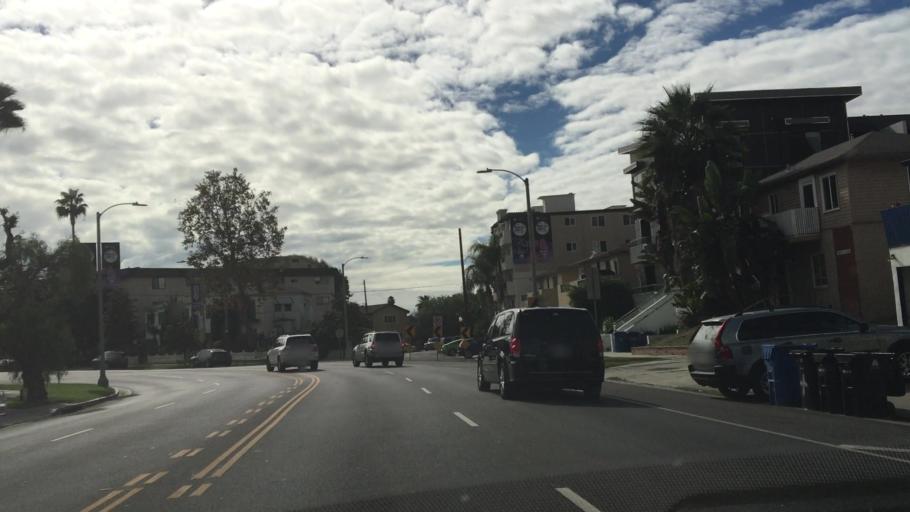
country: US
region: California
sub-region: Los Angeles County
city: Century City
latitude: 34.0519
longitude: -118.4215
